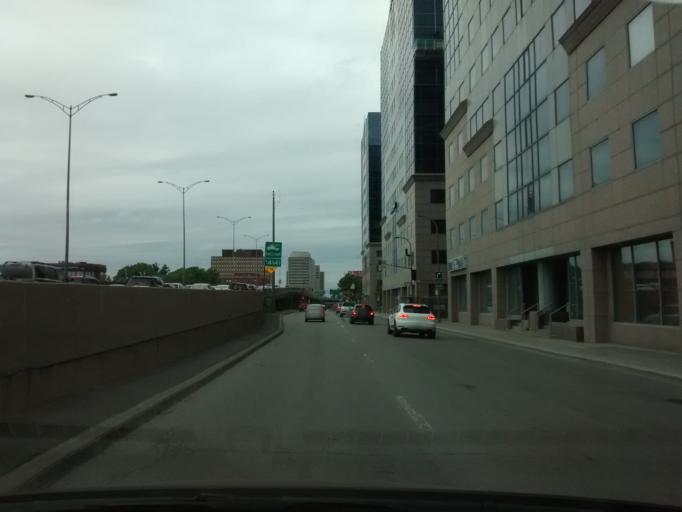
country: CA
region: Quebec
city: Mont-Royal
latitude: 45.5394
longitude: -73.6427
